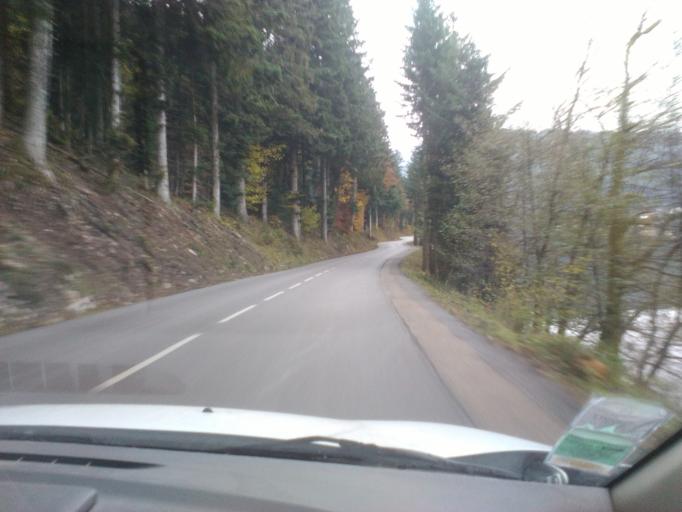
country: FR
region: Lorraine
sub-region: Departement des Vosges
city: Xonrupt-Longemer
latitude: 48.0781
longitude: 6.9498
